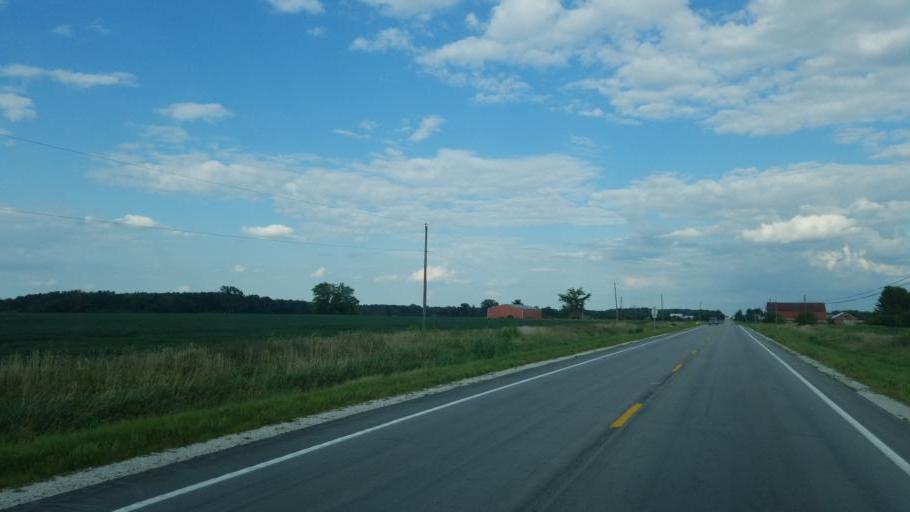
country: US
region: Ohio
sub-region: Sandusky County
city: Gibsonburg
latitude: 41.3413
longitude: -83.2715
